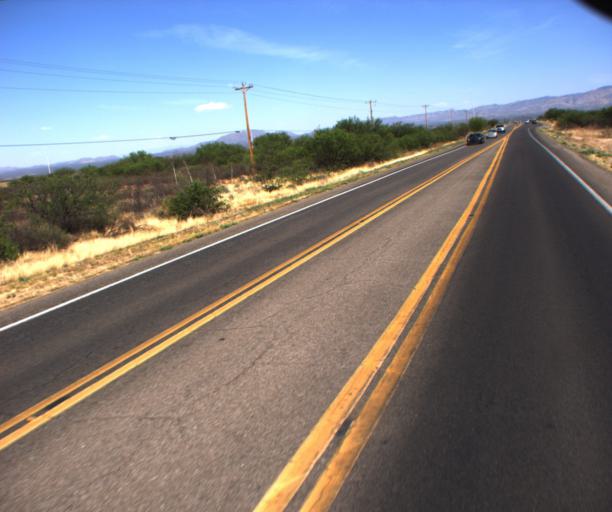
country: US
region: Arizona
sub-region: Cochise County
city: Sierra Vista Southeast
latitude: 31.5531
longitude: -110.1981
